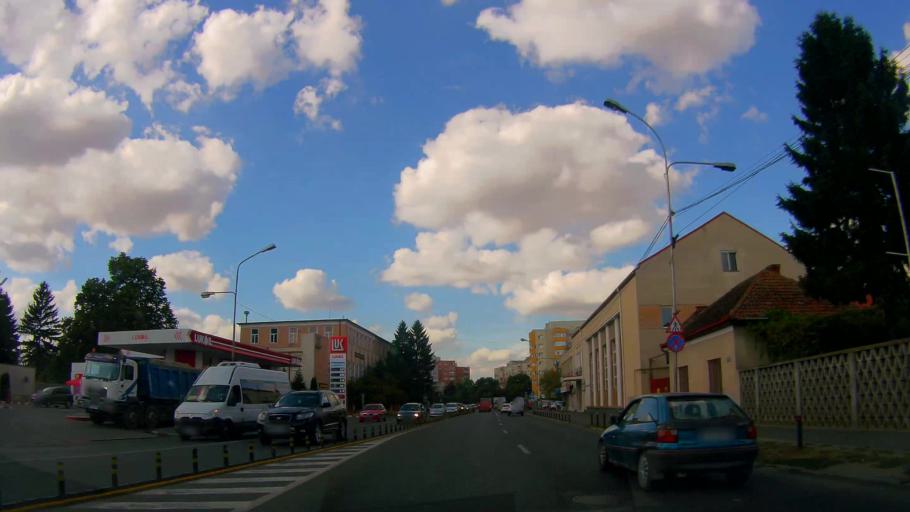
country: RO
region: Satu Mare
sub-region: Municipiul Satu Mare
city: Satu Mare
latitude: 47.7775
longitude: 22.8835
